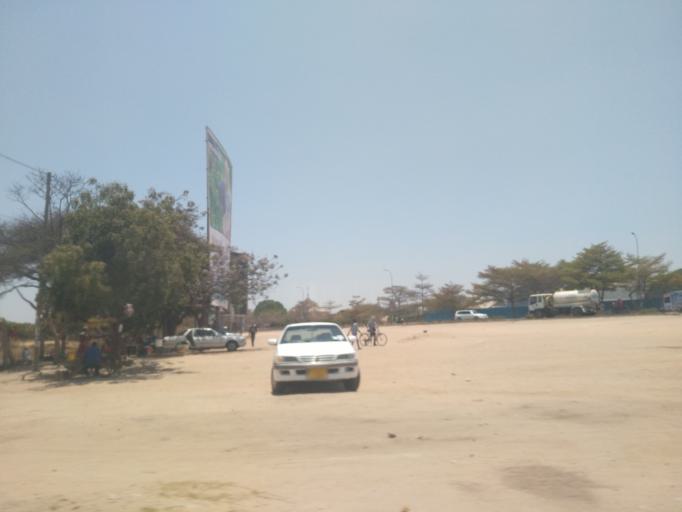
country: TZ
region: Dodoma
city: Dodoma
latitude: -6.1809
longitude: 35.7522
